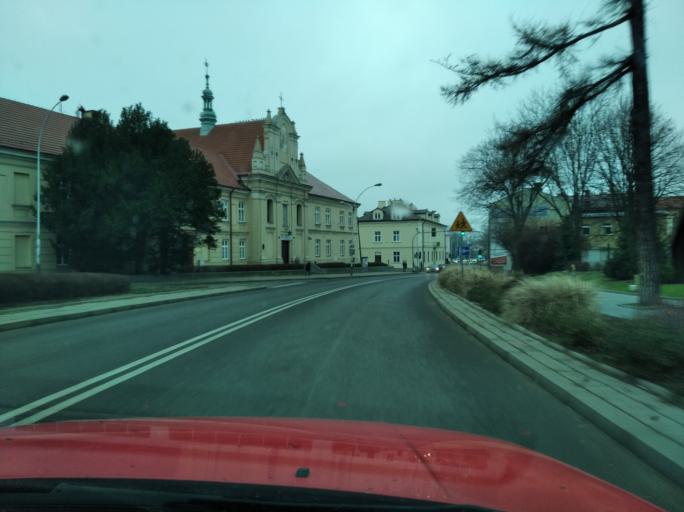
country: PL
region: Subcarpathian Voivodeship
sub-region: Powiat przeworski
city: Przeworsk
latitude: 50.0586
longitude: 22.4913
